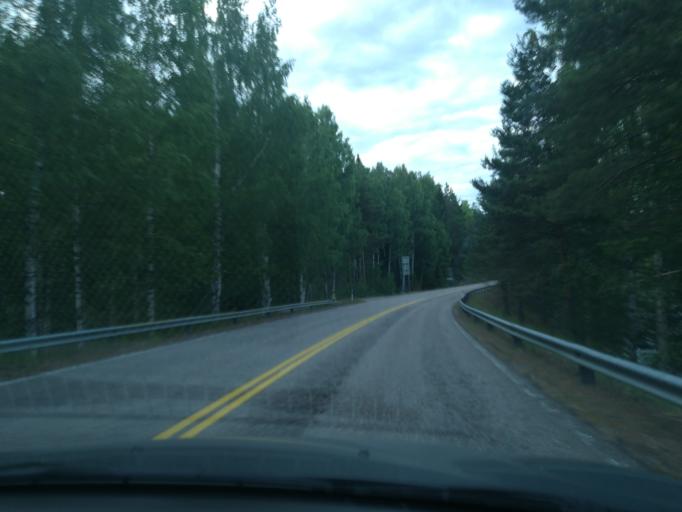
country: FI
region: Southern Savonia
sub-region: Mikkeli
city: Puumala
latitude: 61.5538
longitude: 27.9625
